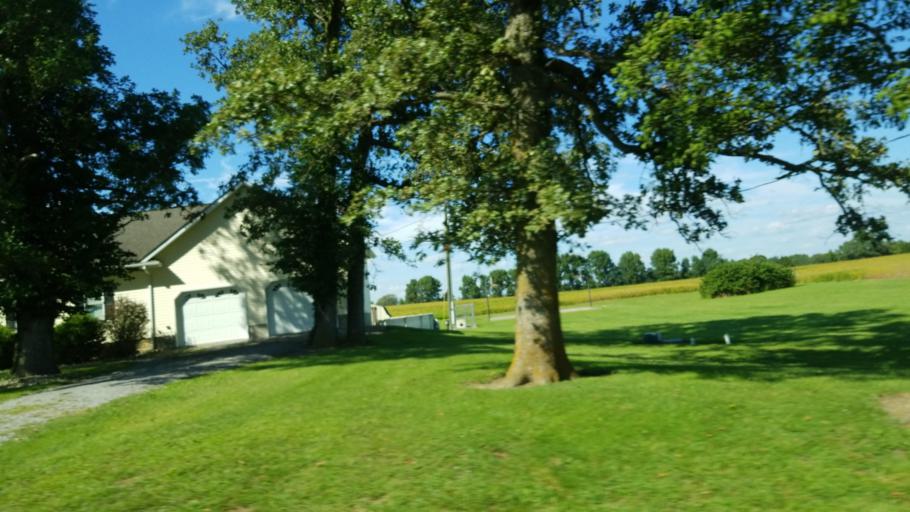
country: US
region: Illinois
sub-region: Williamson County
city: Johnston City
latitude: 37.7905
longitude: -88.7754
